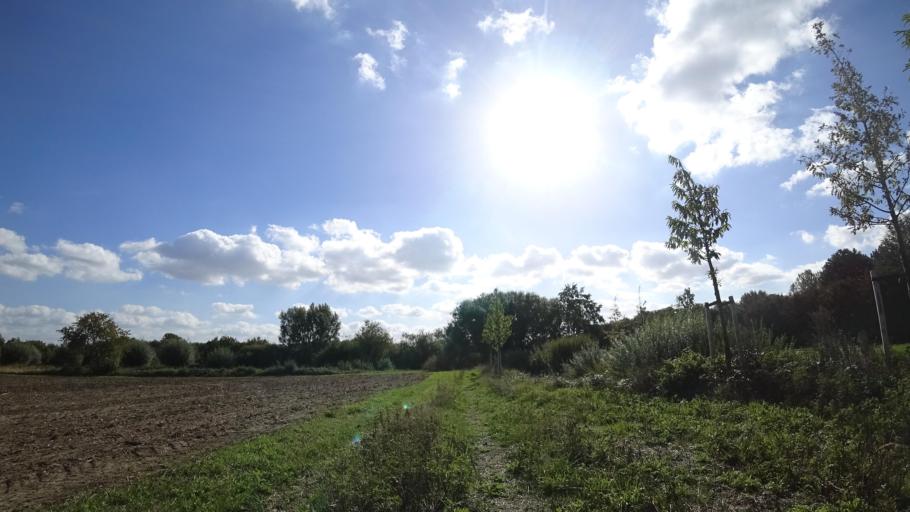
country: DE
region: North Rhine-Westphalia
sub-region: Regierungsbezirk Detmold
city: Rheda-Wiedenbruck
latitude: 51.8642
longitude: 8.2999
